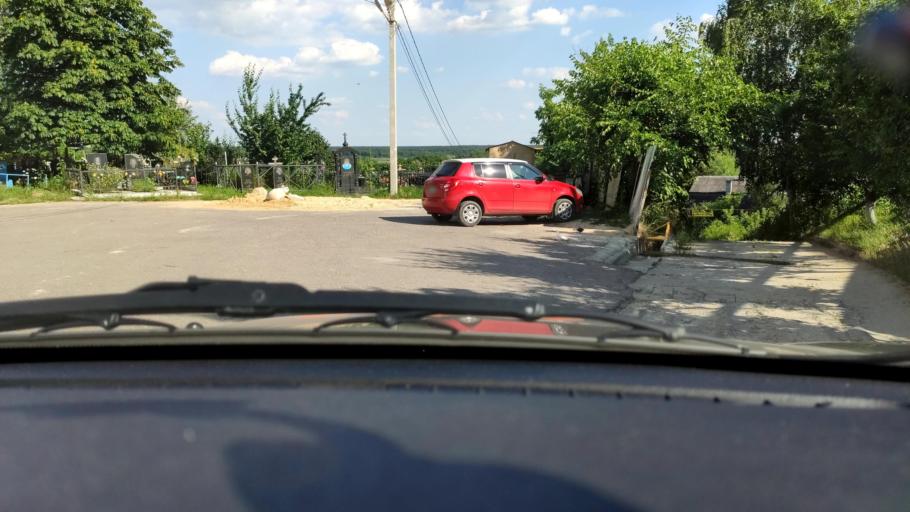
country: RU
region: Voronezj
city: Ramon'
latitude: 51.8207
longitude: 39.2775
